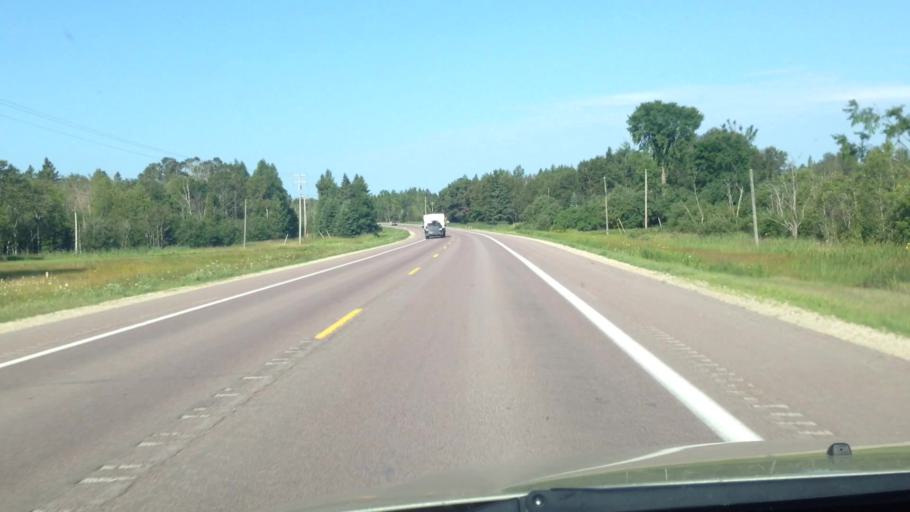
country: US
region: Michigan
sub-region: Schoolcraft County
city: Manistique
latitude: 45.9907
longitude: -86.0853
